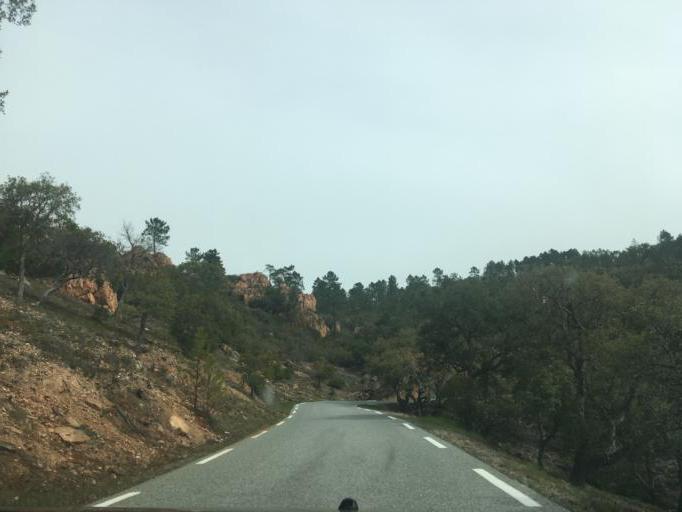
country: FR
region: Provence-Alpes-Cote d'Azur
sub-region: Departement du Var
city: Bagnols-en-Foret
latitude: 43.5175
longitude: 6.6485
